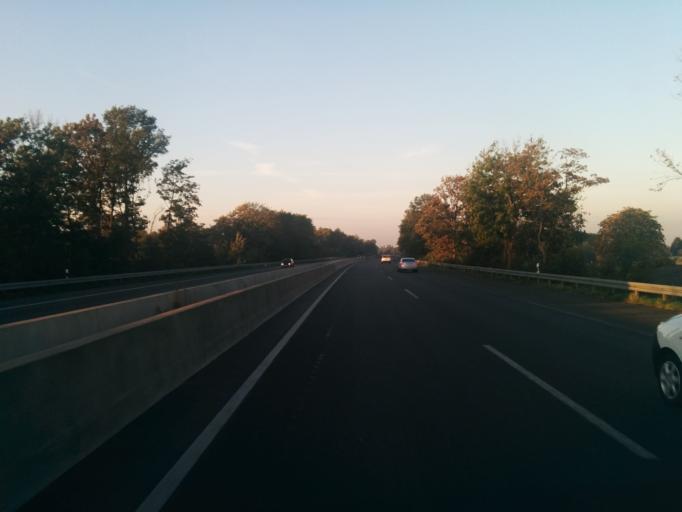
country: DE
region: North Rhine-Westphalia
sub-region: Regierungsbezirk Dusseldorf
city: Ratingen
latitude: 51.3616
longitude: 6.8767
